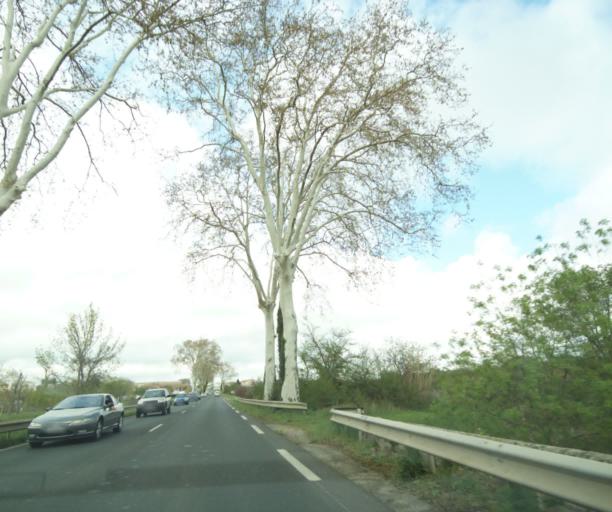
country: FR
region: Languedoc-Roussillon
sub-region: Departement de l'Herault
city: Fabregues
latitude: 43.5546
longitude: 3.7897
